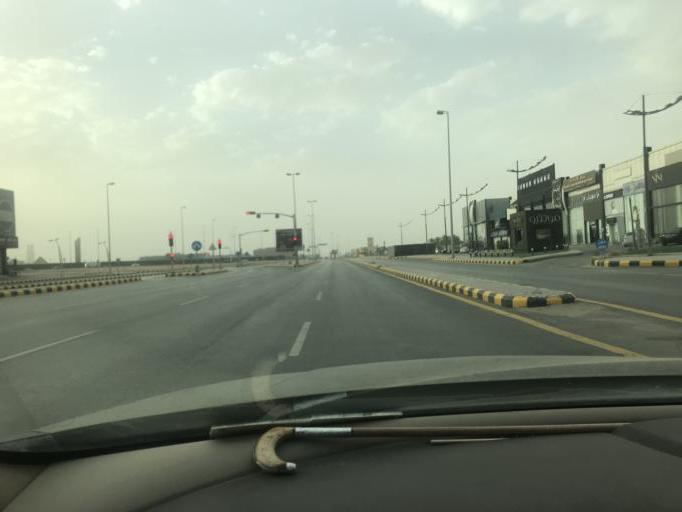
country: SA
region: Ar Riyad
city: Riyadh
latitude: 24.7972
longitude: 46.6548
